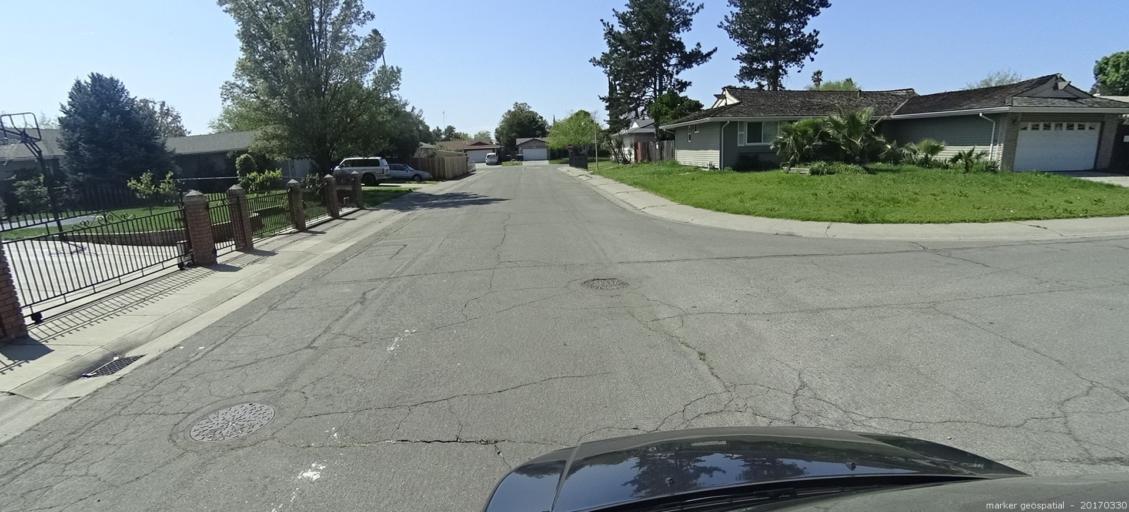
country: US
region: California
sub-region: Sacramento County
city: Florin
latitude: 38.4649
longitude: -121.4236
